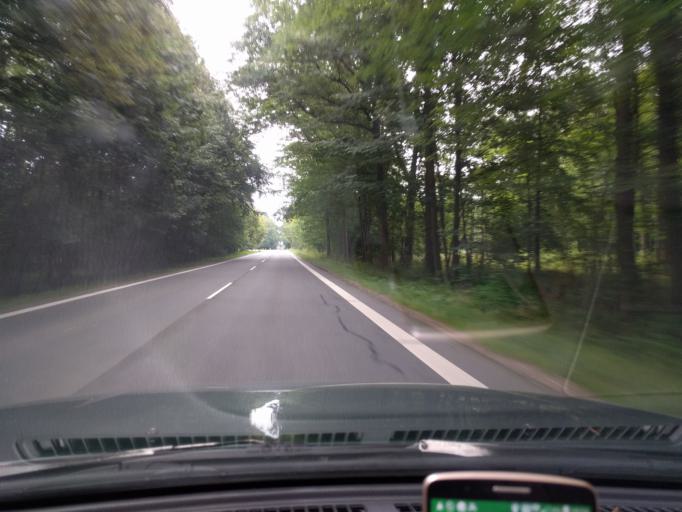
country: DK
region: Zealand
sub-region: Naestved Kommune
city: Fuglebjerg
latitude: 55.2321
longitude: 11.4852
